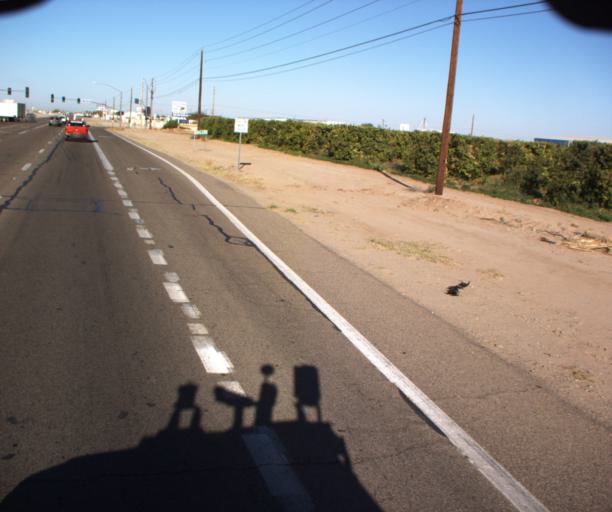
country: US
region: Arizona
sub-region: Yuma County
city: Yuma
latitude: 32.6698
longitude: -114.5712
